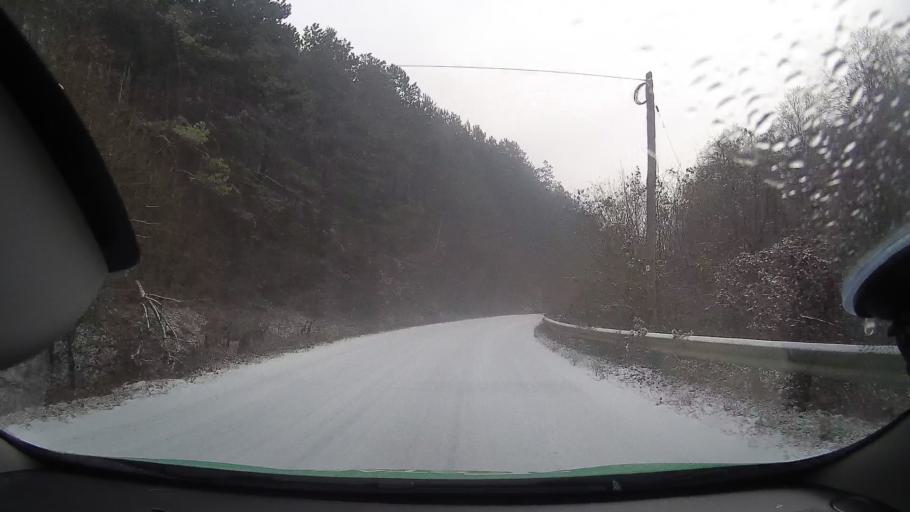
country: RO
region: Alba
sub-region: Comuna Livezile
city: Livezile
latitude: 46.3736
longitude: 23.5855
